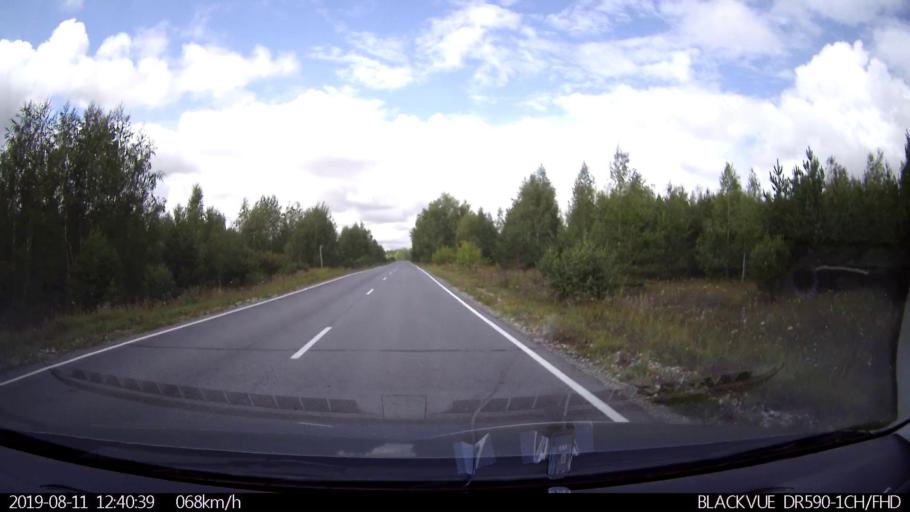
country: RU
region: Ulyanovsk
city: Ignatovka
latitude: 53.8400
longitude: 47.7775
